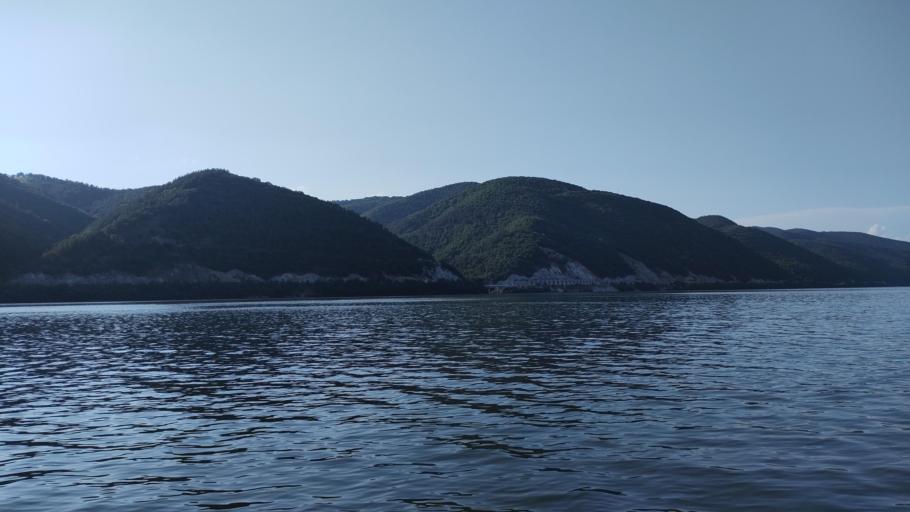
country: RO
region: Mehedinti
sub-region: Comuna Dubova
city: Dubova
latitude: 44.5350
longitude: 22.2155
